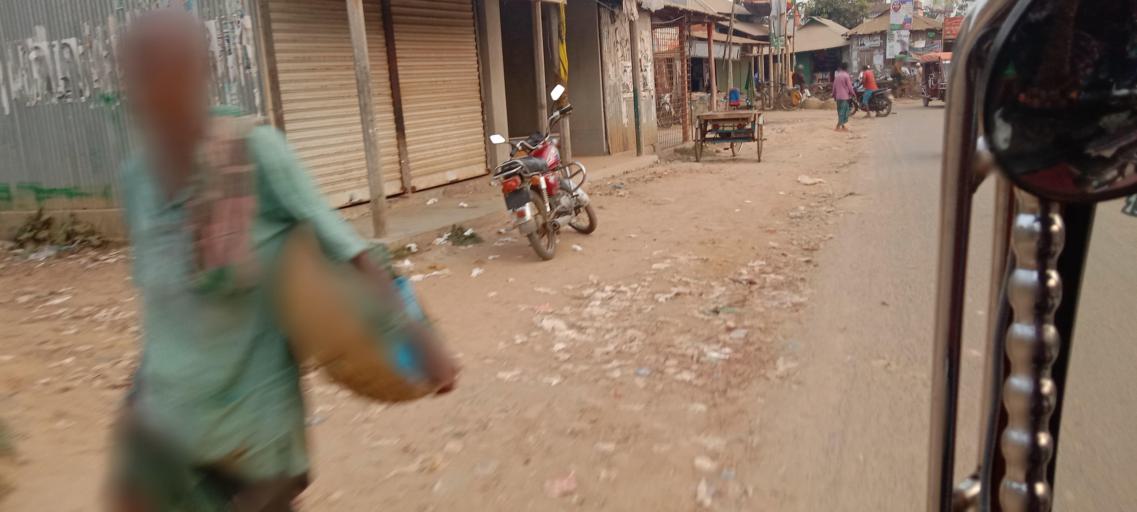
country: BD
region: Dhaka
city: Sakhipur
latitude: 24.4275
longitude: 90.2640
